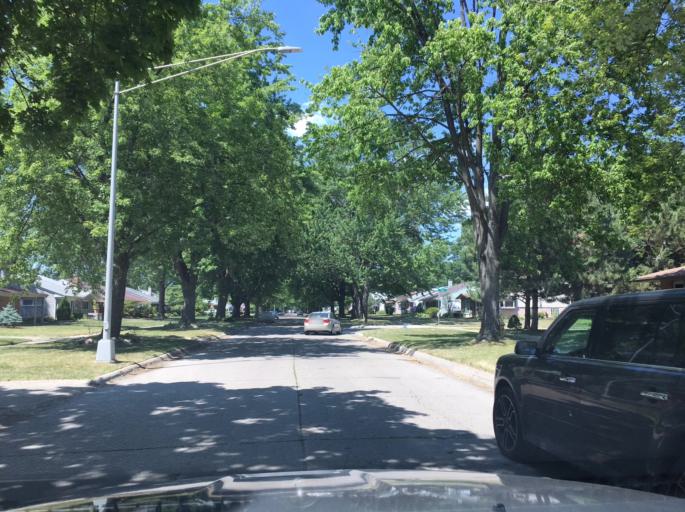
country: US
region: Michigan
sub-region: Macomb County
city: Clinton
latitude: 42.5625
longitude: -82.9012
